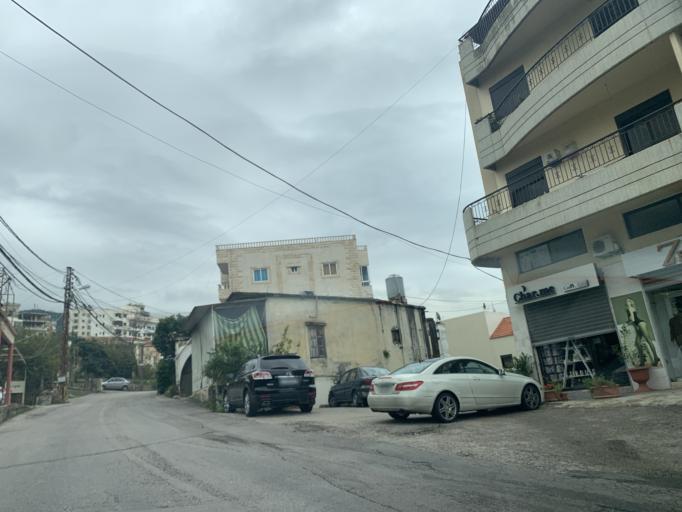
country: LB
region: Mont-Liban
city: Djounie
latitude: 34.0443
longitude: 35.6353
